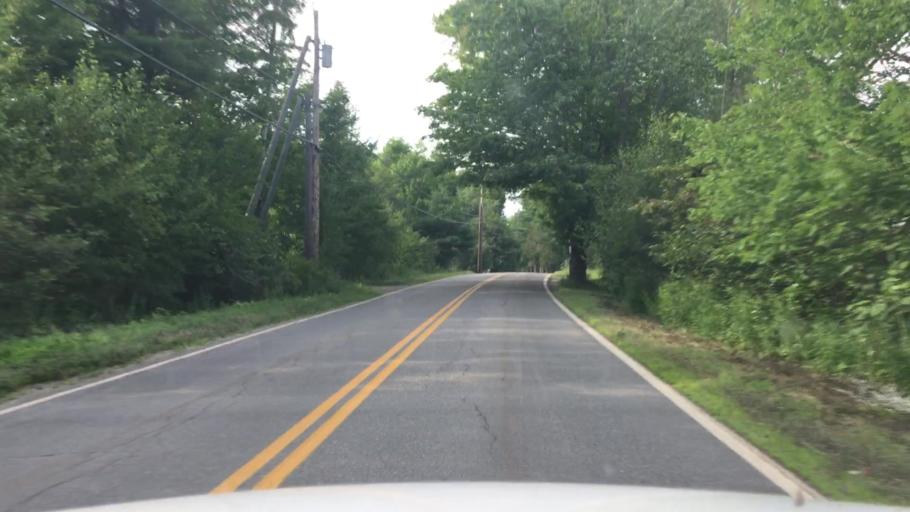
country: US
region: Maine
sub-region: Lincoln County
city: Waldoboro
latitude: 44.1497
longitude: -69.3742
